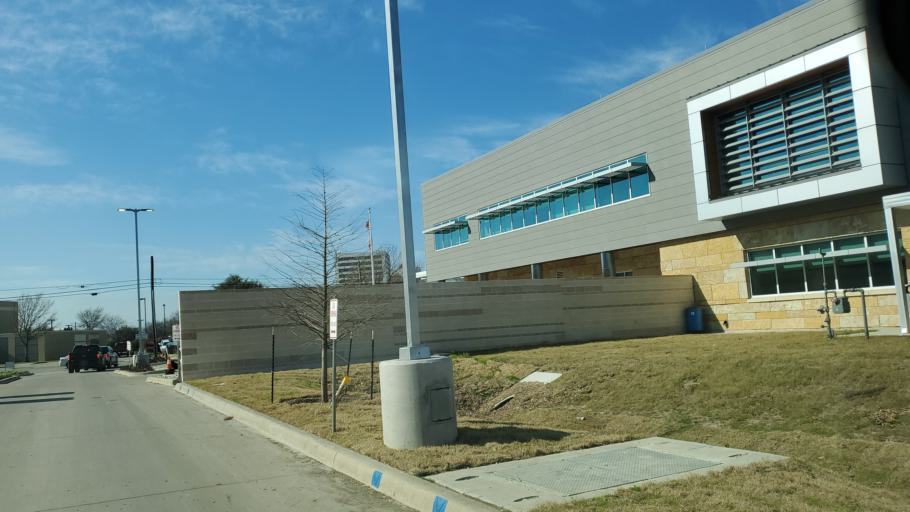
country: US
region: Texas
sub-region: Dallas County
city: Richardson
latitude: 32.9500
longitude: -96.7283
